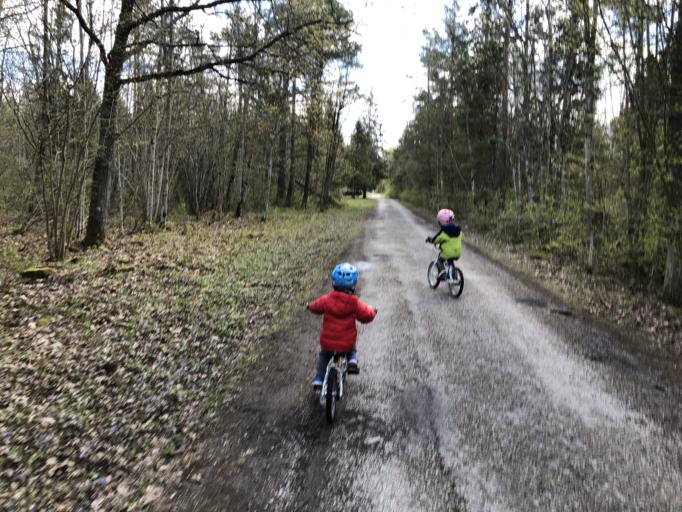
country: EE
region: Harju
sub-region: Harku vald
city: Tabasalu
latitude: 59.4373
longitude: 24.5351
